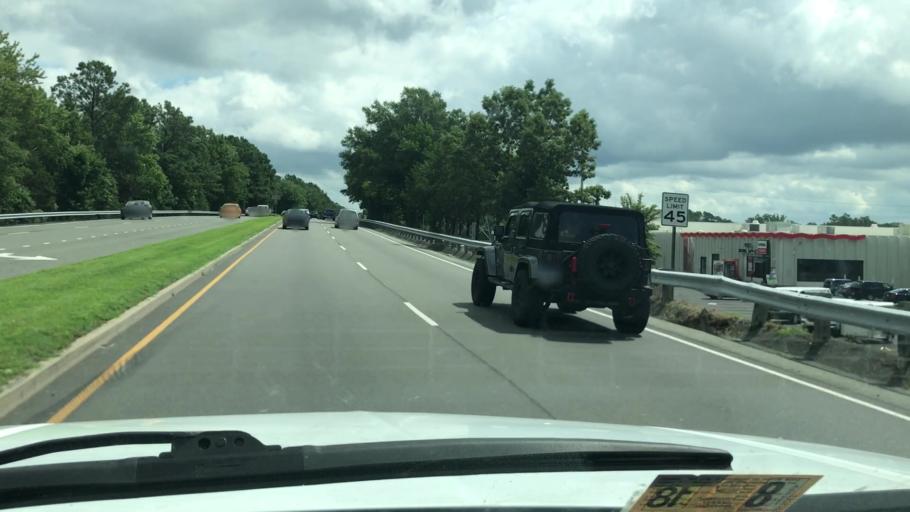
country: US
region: Virginia
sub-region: Henrico County
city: Laurel
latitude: 37.6333
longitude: -77.5063
